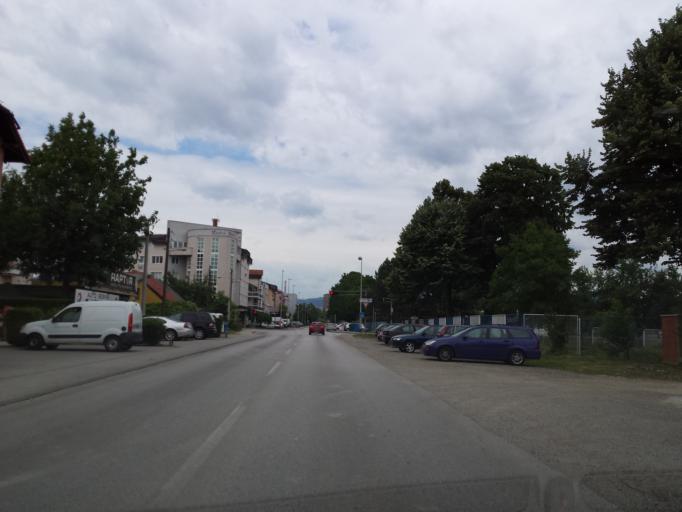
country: HR
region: Grad Zagreb
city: Novi Zagreb
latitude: 45.7823
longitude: 15.9662
